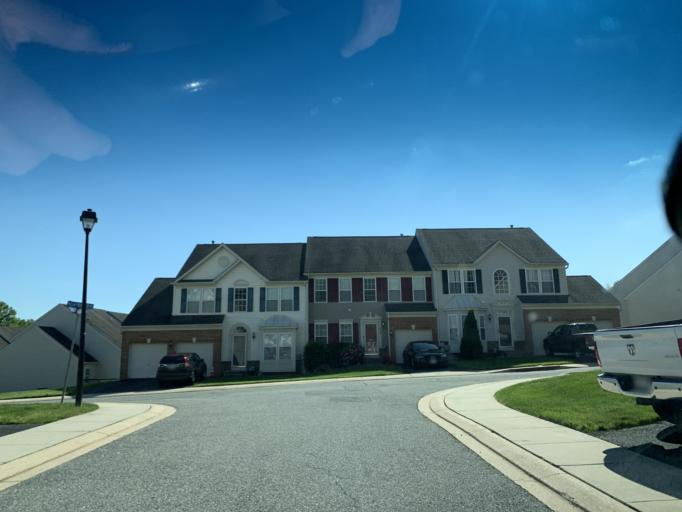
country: US
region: Maryland
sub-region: Harford County
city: Perryman
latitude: 39.4975
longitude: -76.2168
